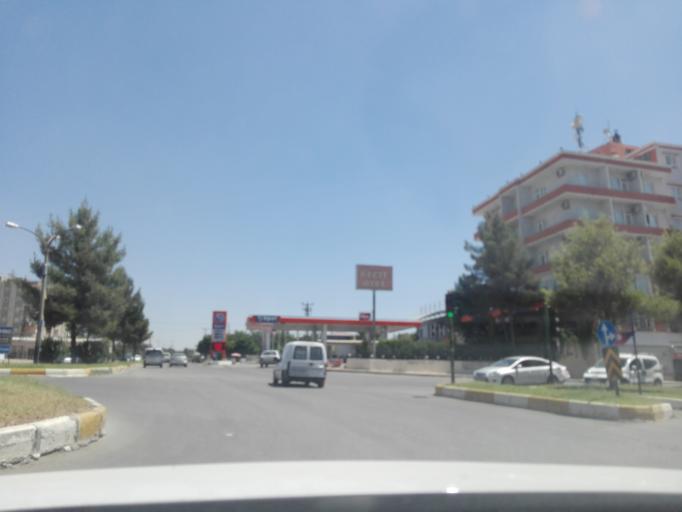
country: TR
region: Batman
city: Batman
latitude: 37.8860
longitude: 41.1366
